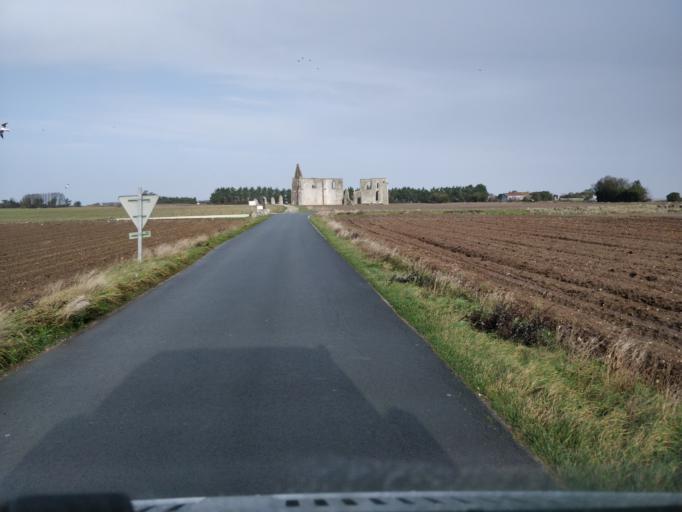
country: FR
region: Poitou-Charentes
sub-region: Departement de la Charente-Maritime
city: La Flotte
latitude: 46.1835
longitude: -1.2982
